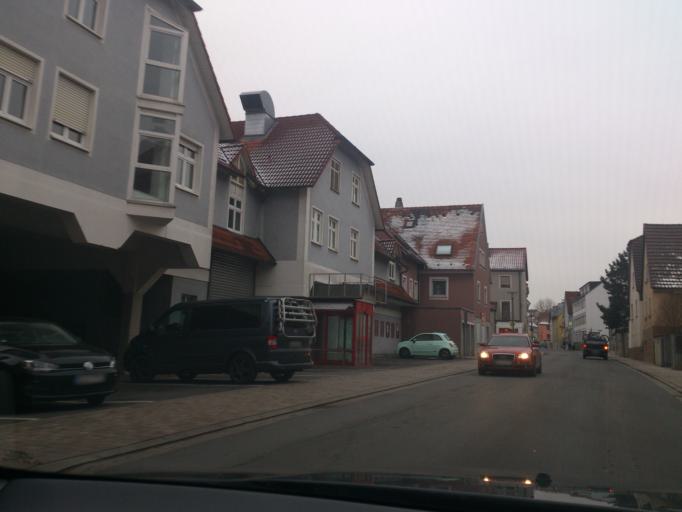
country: DE
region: Bavaria
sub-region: Regierungsbezirk Unterfranken
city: Hochberg
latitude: 49.7838
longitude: 9.8802
